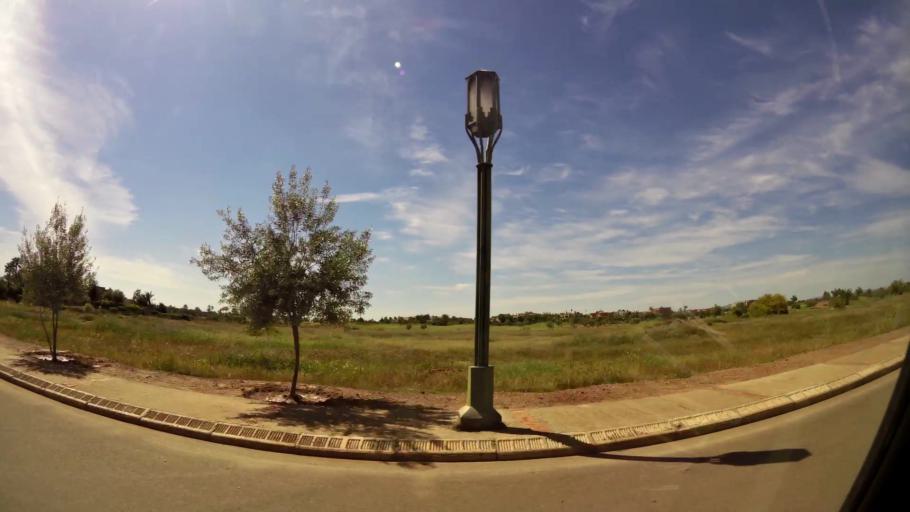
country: MA
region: Marrakech-Tensift-Al Haouz
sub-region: Marrakech
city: Marrakesh
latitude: 31.6144
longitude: -7.9293
